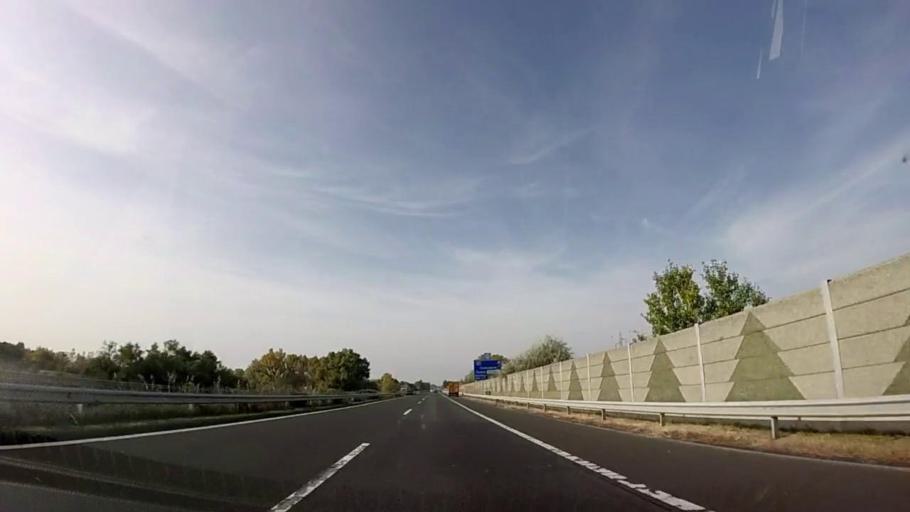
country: HU
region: Somogy
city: Siofok
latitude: 46.8999
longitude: 18.0693
